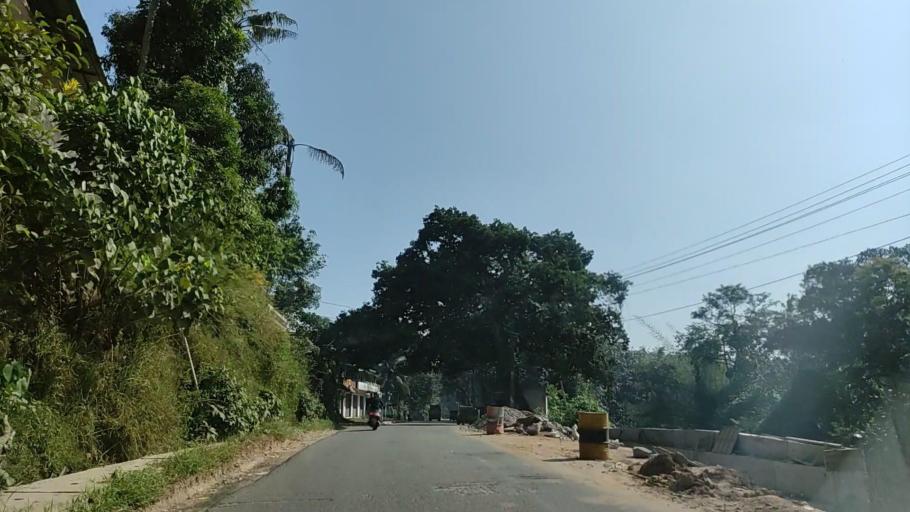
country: IN
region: Kerala
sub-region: Kollam
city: Punalur
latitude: 8.9035
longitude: 76.8699
